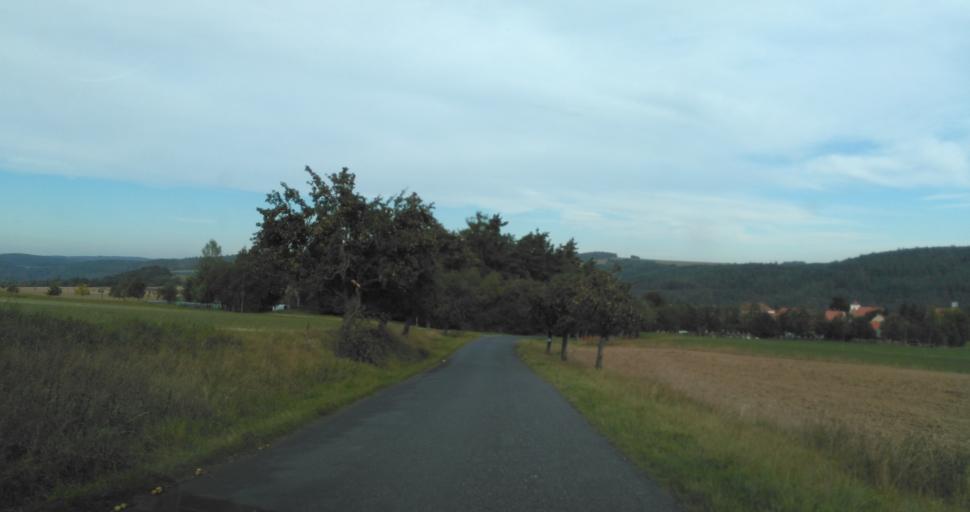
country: CZ
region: Plzensky
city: Zbiroh
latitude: 49.9598
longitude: 13.7705
